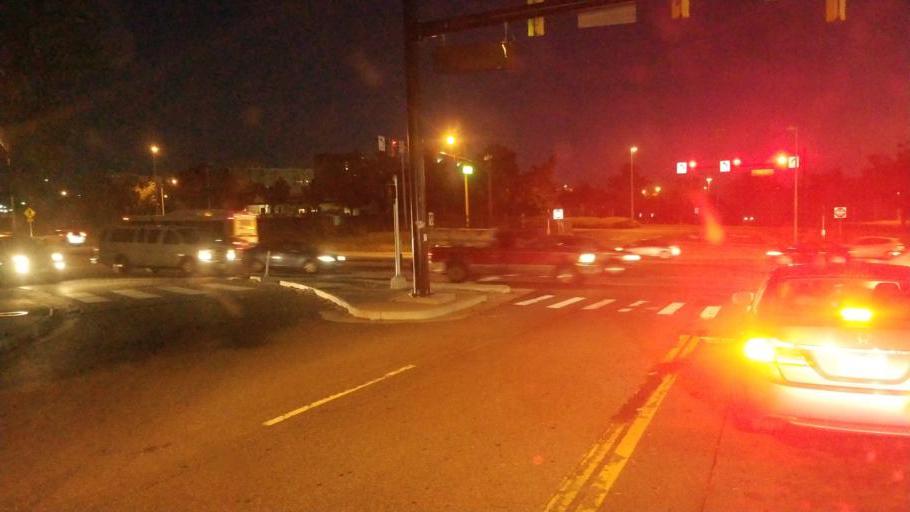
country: US
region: Virginia
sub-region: Fairfax County
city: Lincolnia
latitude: 38.8139
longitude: -77.1340
